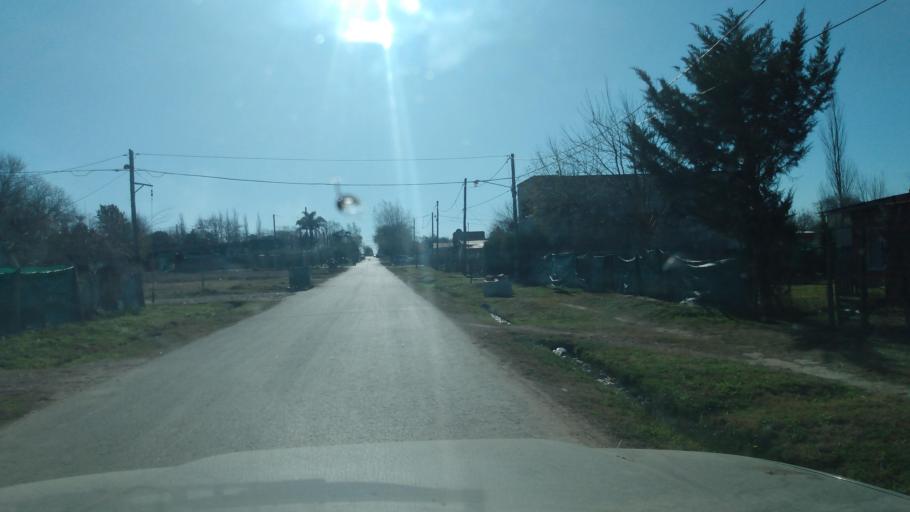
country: AR
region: Buenos Aires
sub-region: Partido de Lujan
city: Lujan
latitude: -34.5700
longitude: -59.0809
